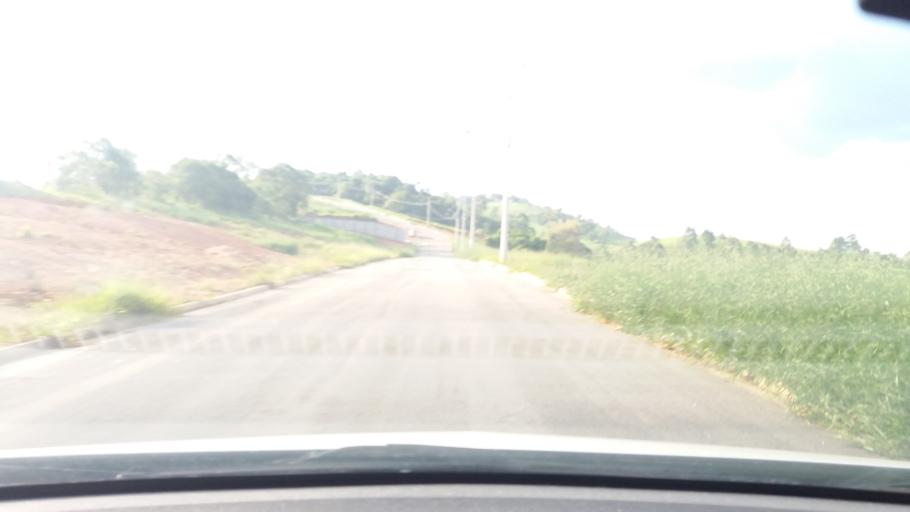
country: BR
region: Sao Paulo
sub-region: Bom Jesus Dos Perdoes
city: Bom Jesus dos Perdoes
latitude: -23.1533
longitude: -46.4757
